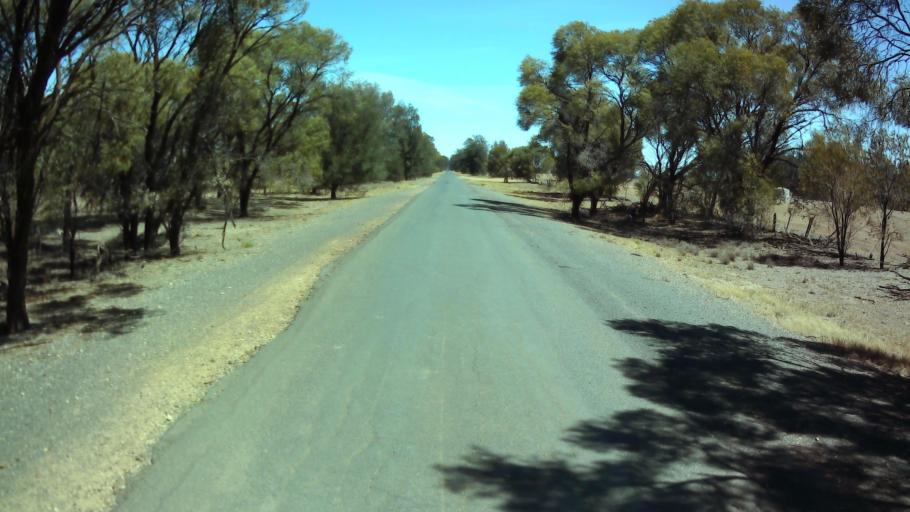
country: AU
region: New South Wales
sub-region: Weddin
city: Grenfell
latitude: -33.8720
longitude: 147.6917
